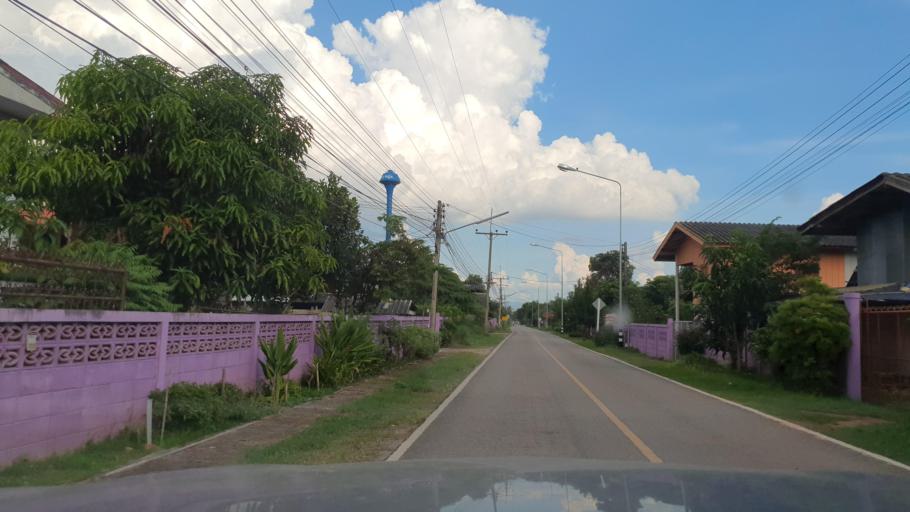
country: TH
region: Phayao
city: Phayao
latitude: 19.1801
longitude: 99.8373
